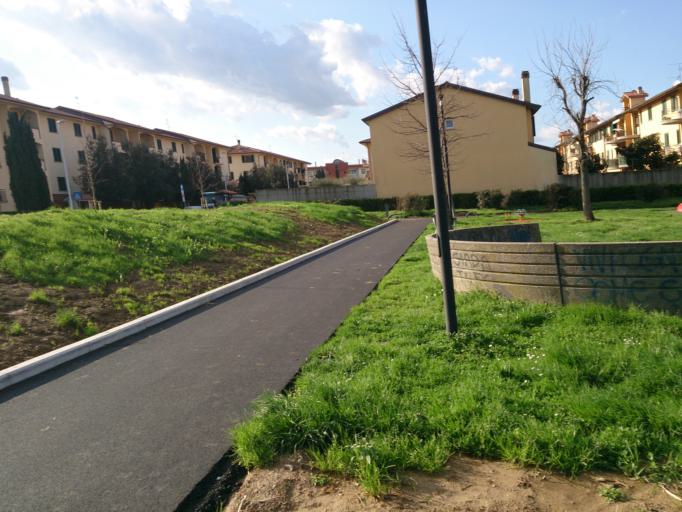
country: IT
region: Tuscany
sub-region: Provincia di Prato
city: Fornacelle
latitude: 43.8886
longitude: 11.0474
